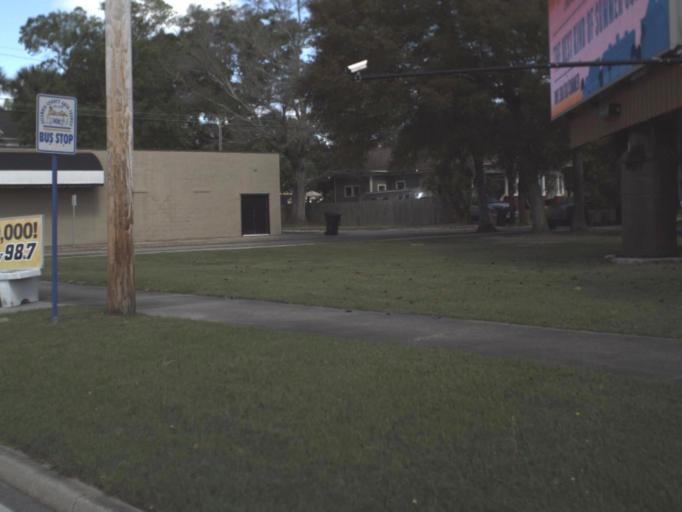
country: US
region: Florida
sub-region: Escambia County
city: Pensacola
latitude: 30.4114
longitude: -87.2291
